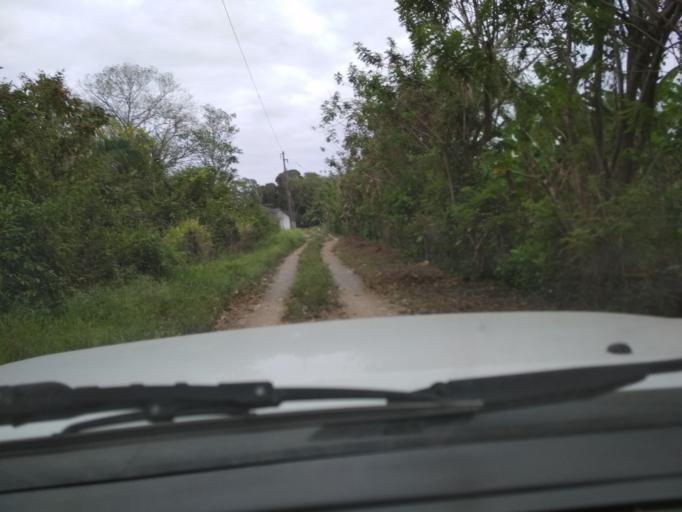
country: MX
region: Veracruz
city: El Tejar
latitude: 19.0727
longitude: -96.1390
